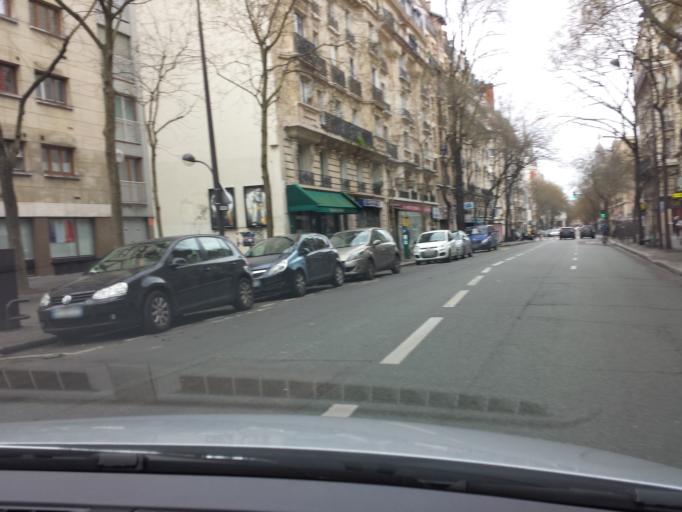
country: FR
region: Ile-de-France
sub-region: Departement du Val-de-Marne
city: Le Kremlin-Bicetre
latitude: 48.8261
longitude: 2.3551
